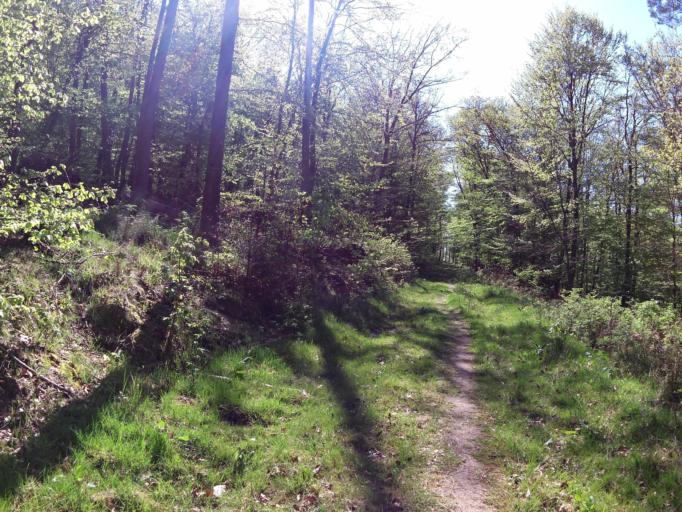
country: DE
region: Thuringia
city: Eisenach
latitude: 50.9731
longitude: 10.2921
